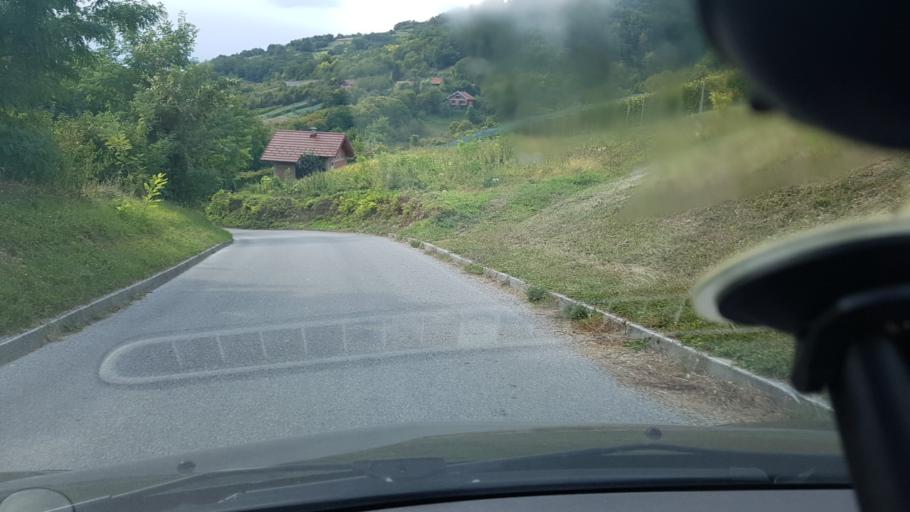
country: HR
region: Krapinsko-Zagorska
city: Radoboj
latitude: 46.1716
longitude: 15.9388
